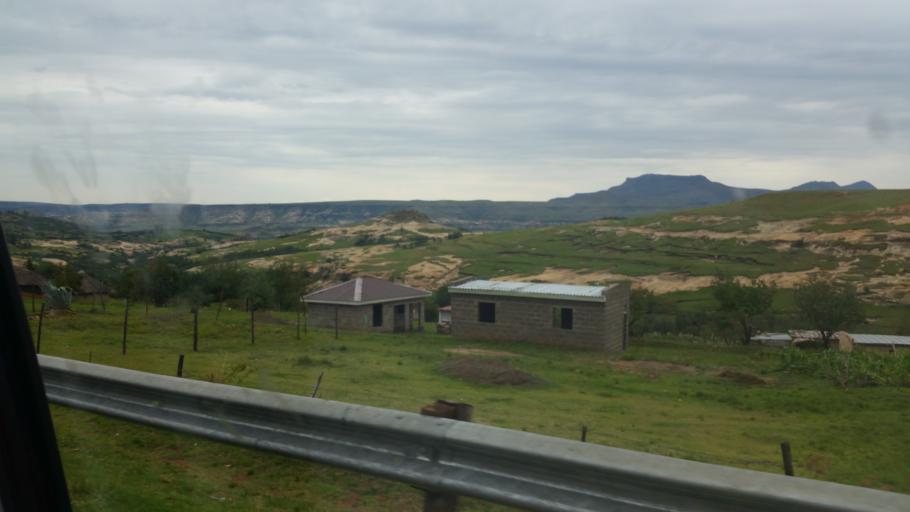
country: LS
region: Berea
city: Teyateyaneng
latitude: -29.1343
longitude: 27.9881
